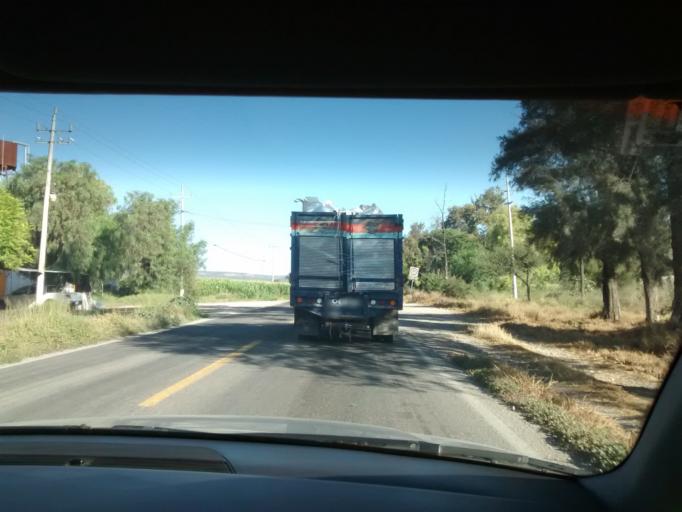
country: MX
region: Puebla
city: San Bartolo Teontepec
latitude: 18.5336
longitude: -97.5261
